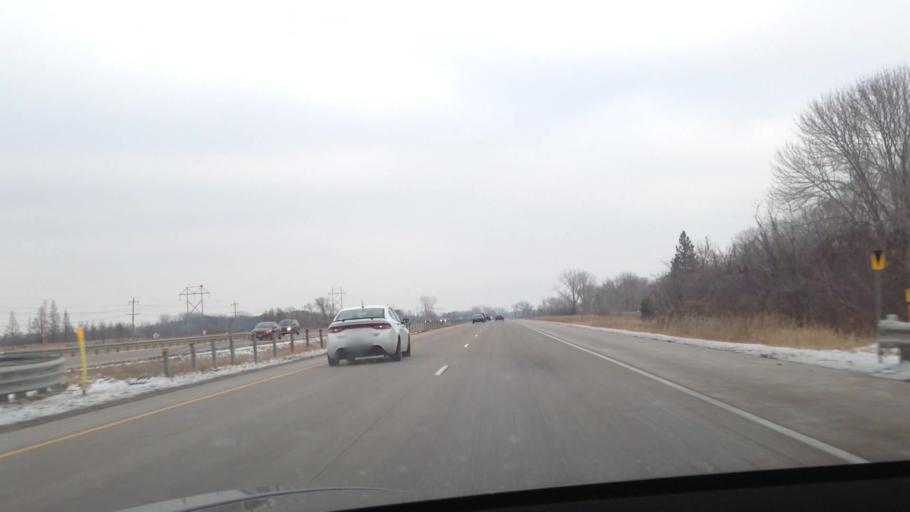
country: US
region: Minnesota
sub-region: Anoka County
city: Centerville
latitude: 45.1929
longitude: -93.0713
